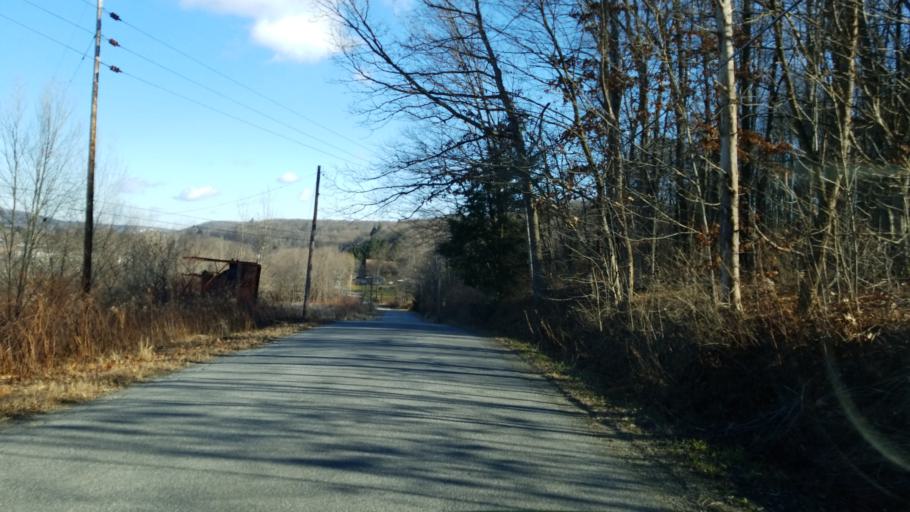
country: US
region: Pennsylvania
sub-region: Clearfield County
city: Hyde
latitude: 40.9873
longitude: -78.4722
